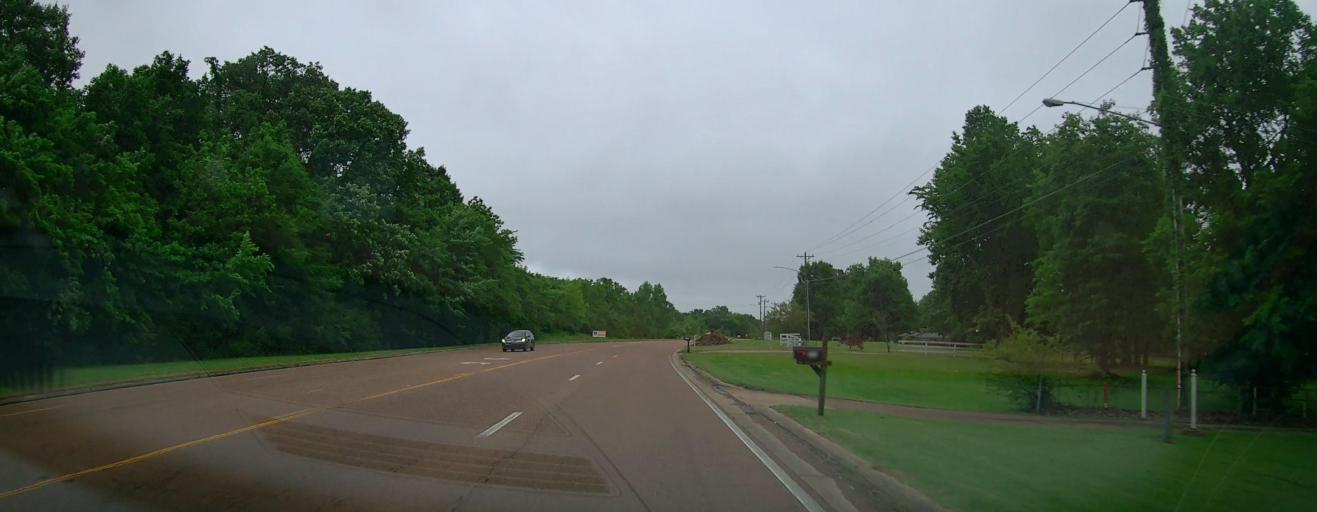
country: US
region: Mississippi
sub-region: De Soto County
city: Olive Branch
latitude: 34.9588
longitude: -89.7955
